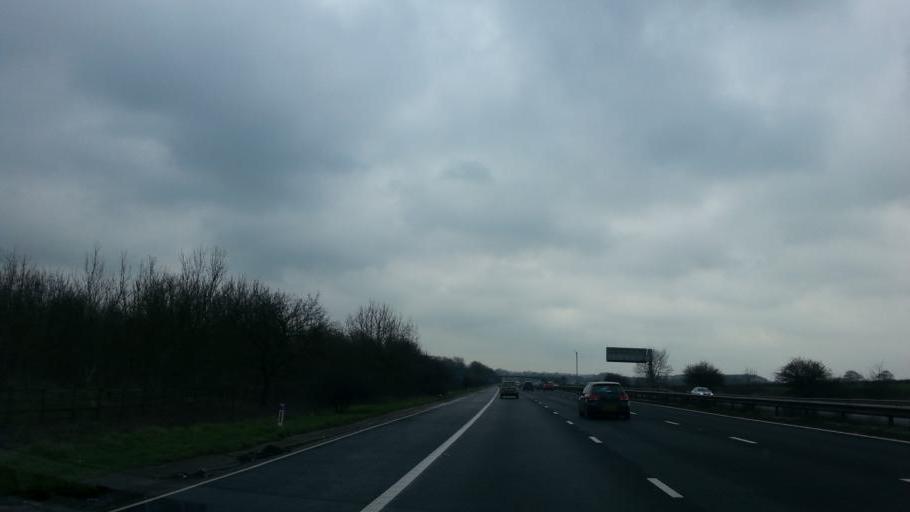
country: GB
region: England
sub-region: South Gloucestershire
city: Alveston
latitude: 51.5609
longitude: -2.5343
